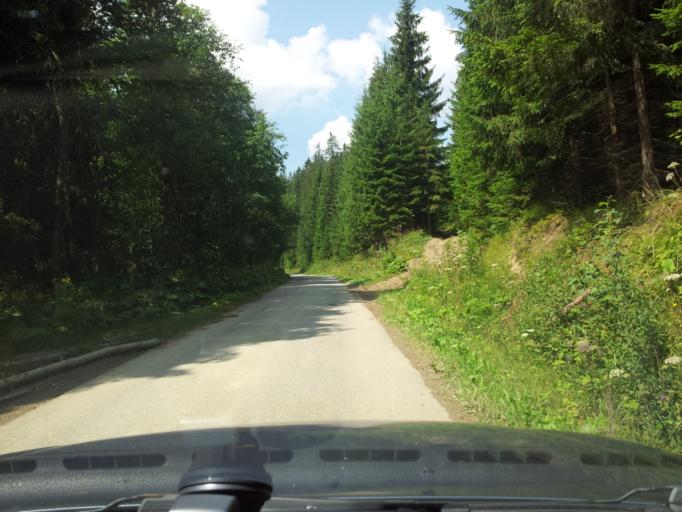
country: SK
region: Zilinsky
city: Oravska Lesna
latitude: 49.3885
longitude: 19.2128
